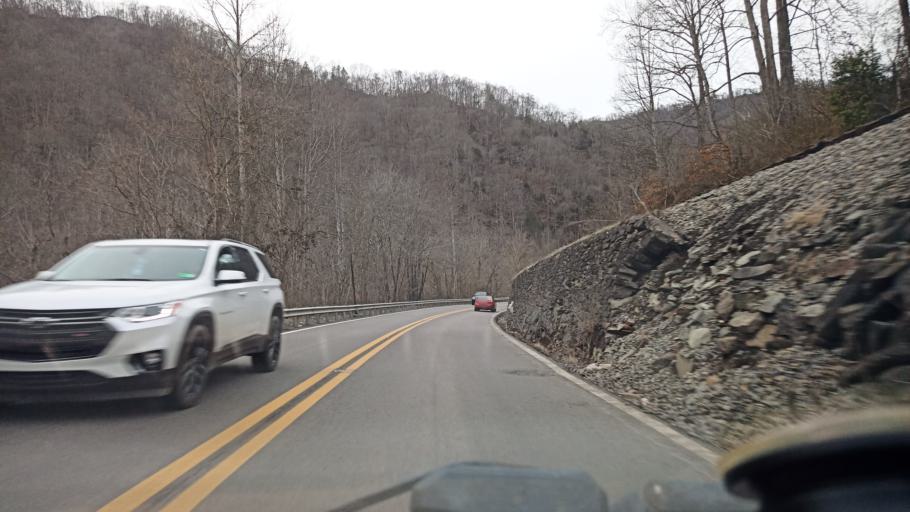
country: US
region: West Virginia
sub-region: Logan County
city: Mallory
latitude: 37.6930
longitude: -81.8693
